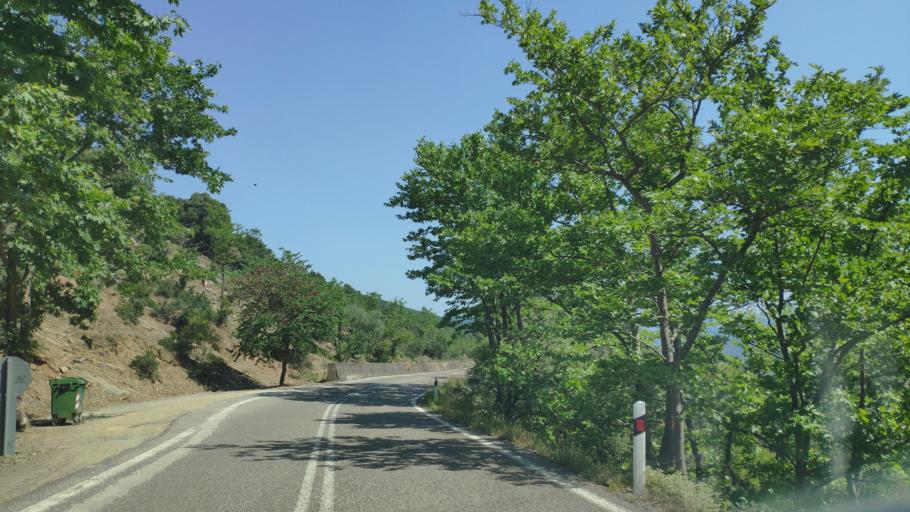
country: GR
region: West Greece
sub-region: Nomos Aitolias kai Akarnanias
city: Lepenou
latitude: 38.7925
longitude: 21.3328
